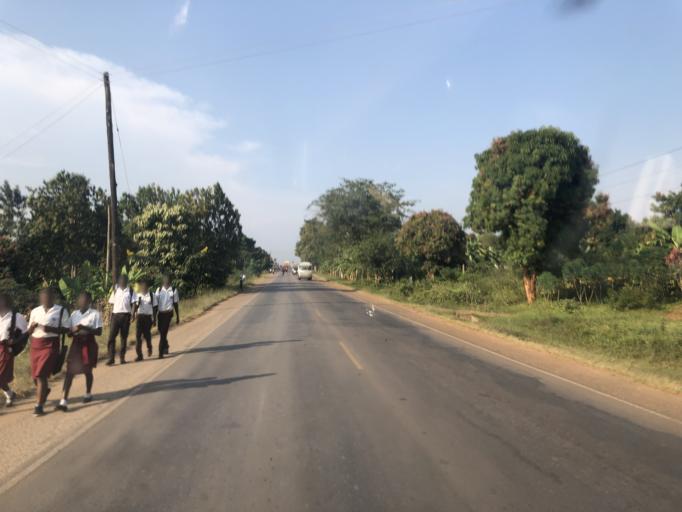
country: UG
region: Central Region
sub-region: Butambala District
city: Gombe
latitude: 0.0734
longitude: 32.1203
